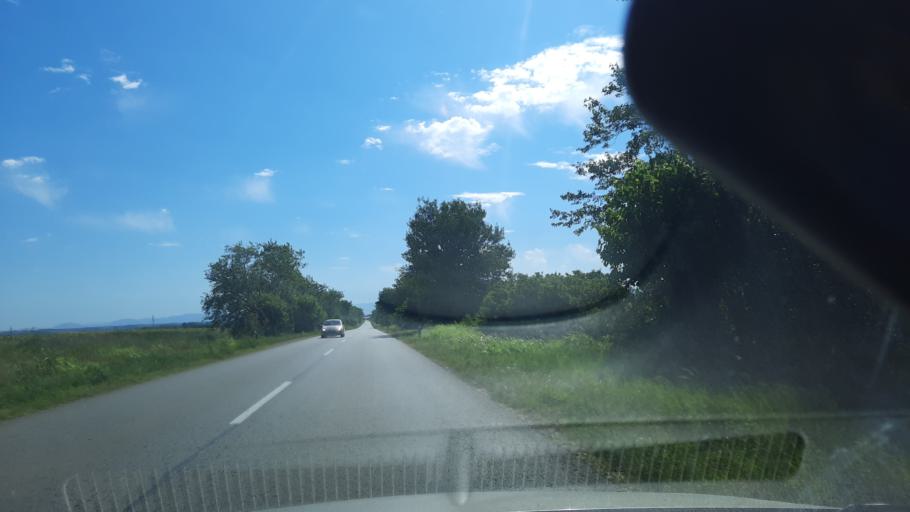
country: RO
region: Caras-Severin
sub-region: Comuna Socol
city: Socol
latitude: 44.8758
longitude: 21.3408
